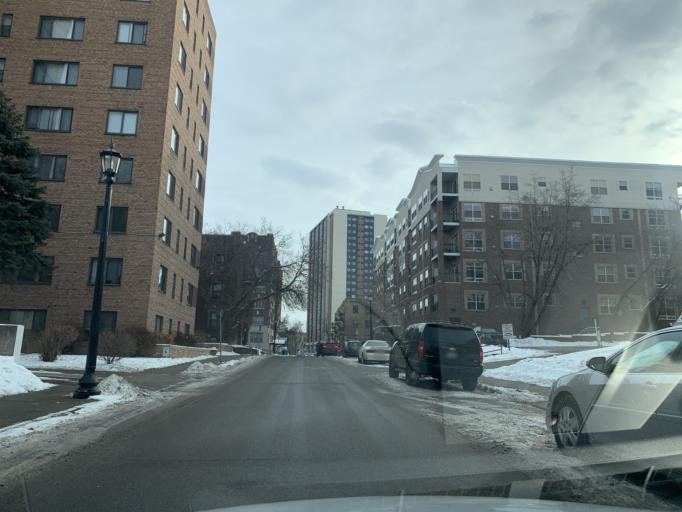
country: US
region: Minnesota
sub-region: Hennepin County
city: Minneapolis
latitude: 44.9671
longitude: -93.2838
